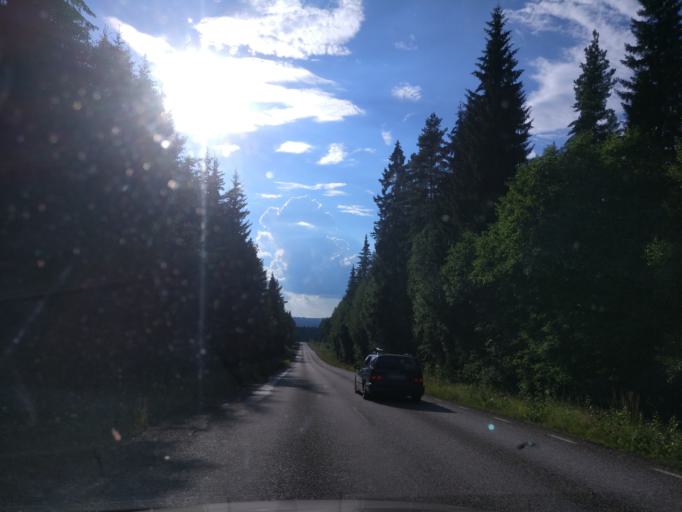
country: SE
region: Dalarna
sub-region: Ludvika Kommun
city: Ludvika
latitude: 60.2651
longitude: 15.0448
